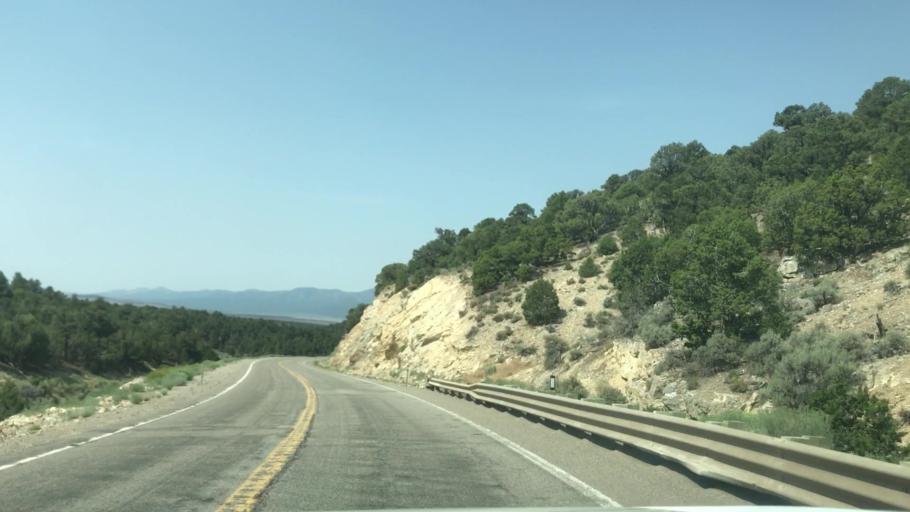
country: US
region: Nevada
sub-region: White Pine County
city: Ely
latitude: 39.0330
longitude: -114.6605
